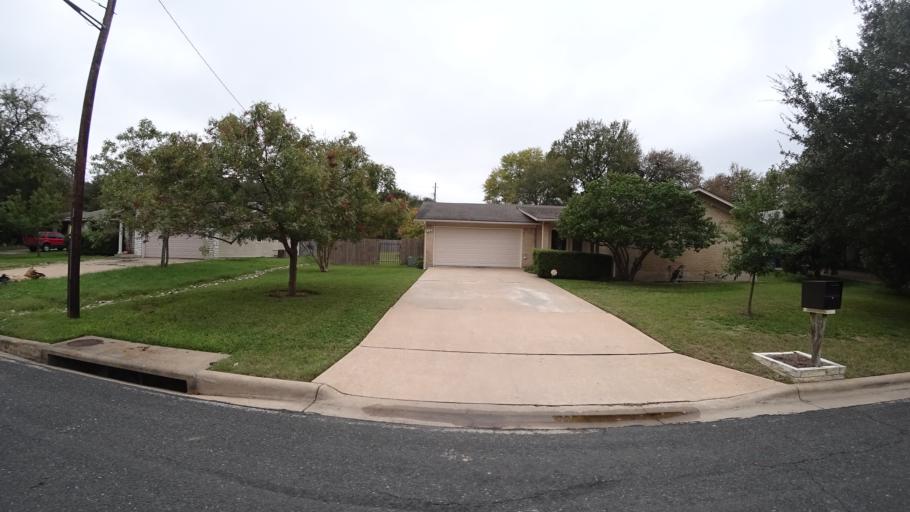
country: US
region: Texas
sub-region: Travis County
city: Barton Creek
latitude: 30.2446
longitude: -97.8886
